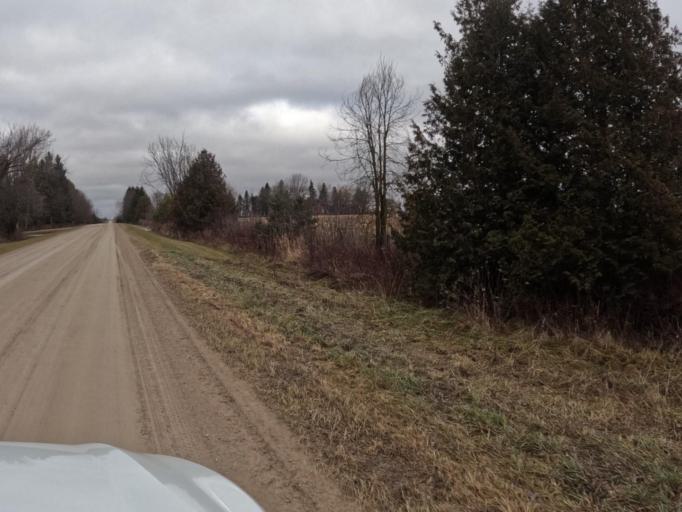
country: CA
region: Ontario
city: Shelburne
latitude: 43.9609
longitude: -80.3993
